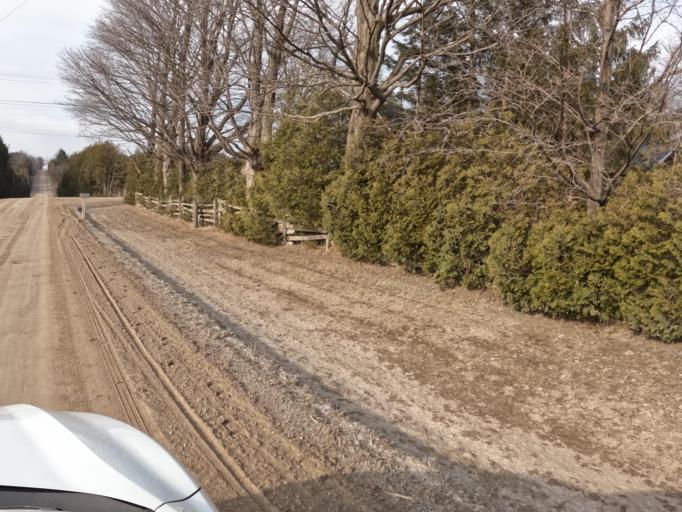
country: CA
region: Ontario
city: Orangeville
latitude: 43.9108
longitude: -80.2702
